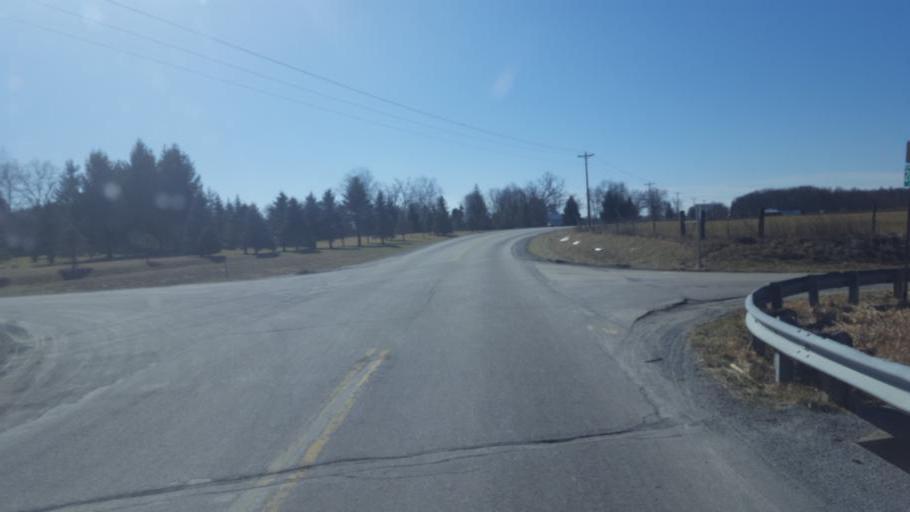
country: US
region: Ohio
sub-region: Hardin County
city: Kenton
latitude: 40.6193
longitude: -83.4999
